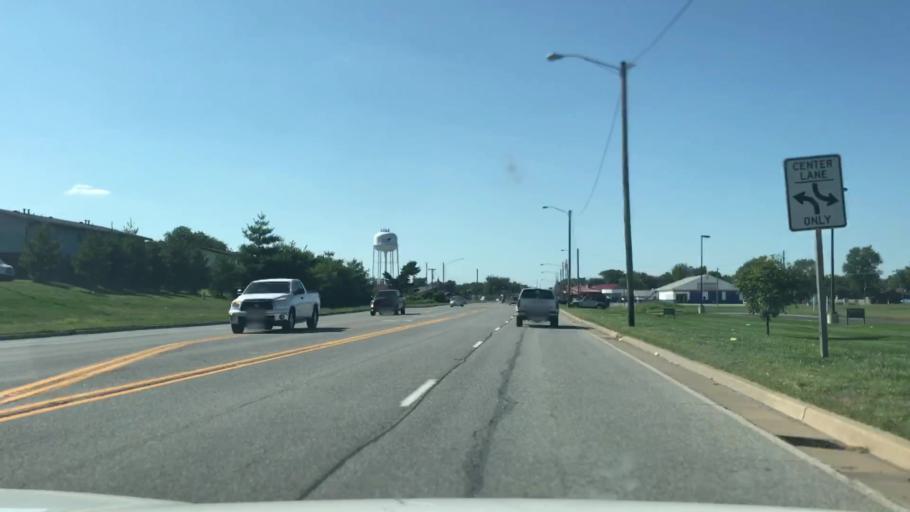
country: US
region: Illinois
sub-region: Madison County
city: Roxana
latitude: 38.8587
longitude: -90.0689
